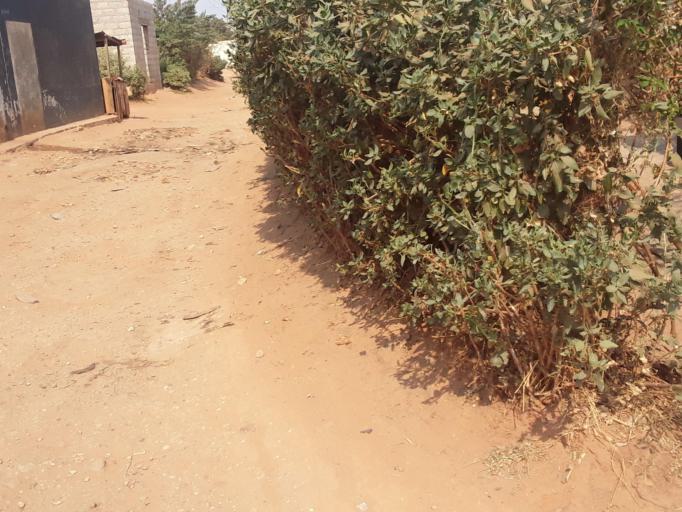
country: ZM
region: Lusaka
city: Lusaka
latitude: -15.3537
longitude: 28.2991
